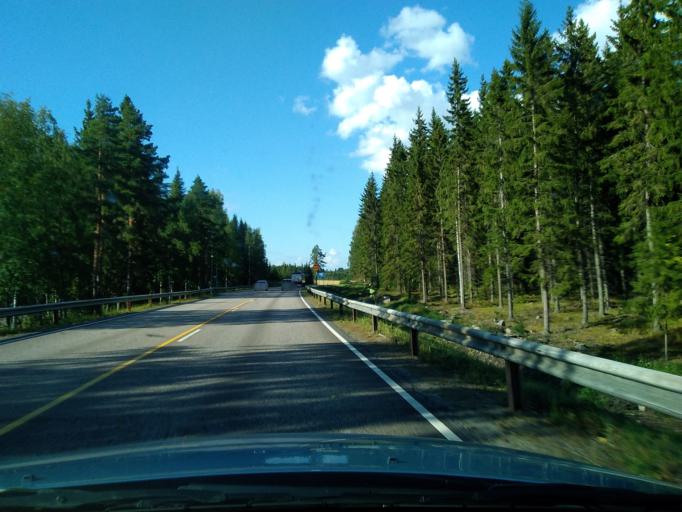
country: FI
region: Central Finland
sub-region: Keuruu
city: Keuruu
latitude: 62.1265
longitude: 24.7366
